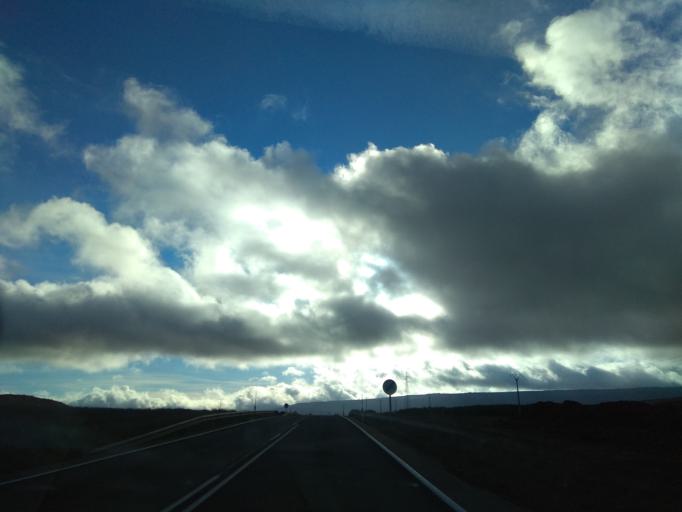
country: ES
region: Castille and Leon
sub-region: Provincia de Palencia
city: Pomar de Valdivia
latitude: 42.7563
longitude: -4.1789
